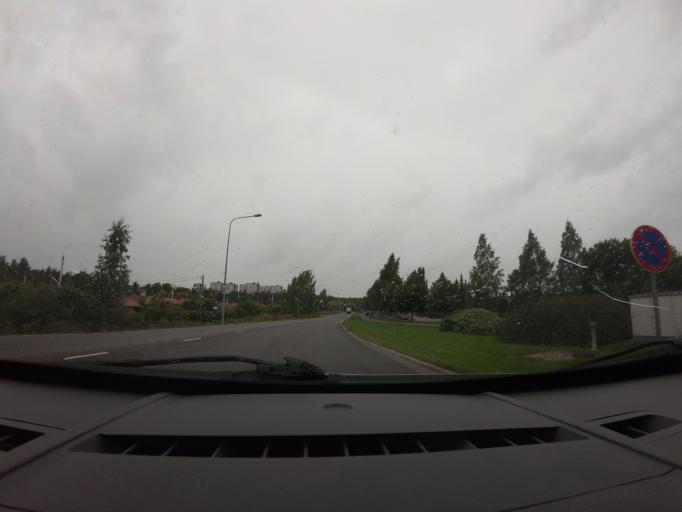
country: FI
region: Varsinais-Suomi
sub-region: Turku
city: Turku
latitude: 60.4217
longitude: 22.3002
